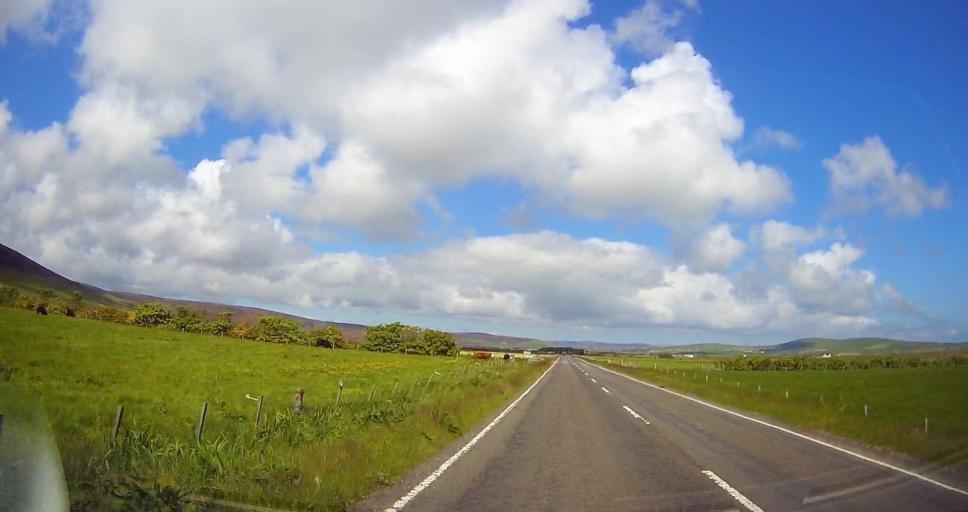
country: GB
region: Scotland
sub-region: Orkney Islands
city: Orkney
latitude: 59.0348
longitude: -3.0900
